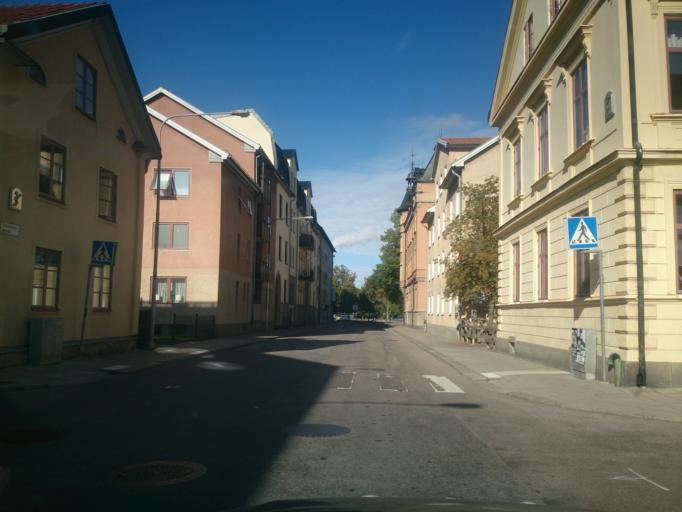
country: SE
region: OEstergoetland
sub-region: Linkopings Kommun
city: Linkoping
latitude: 58.4135
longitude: 15.6279
